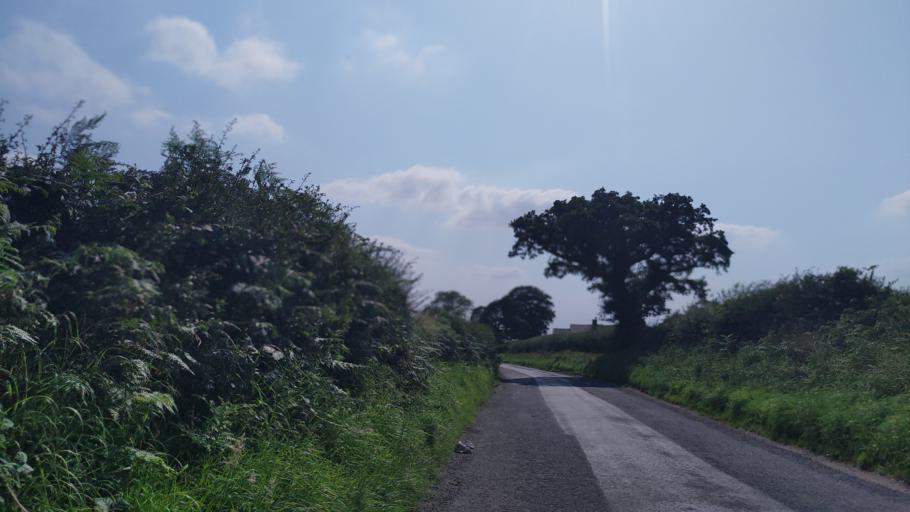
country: GB
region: England
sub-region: Lancashire
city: Clayton-le-Woods
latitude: 53.6978
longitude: -2.6212
